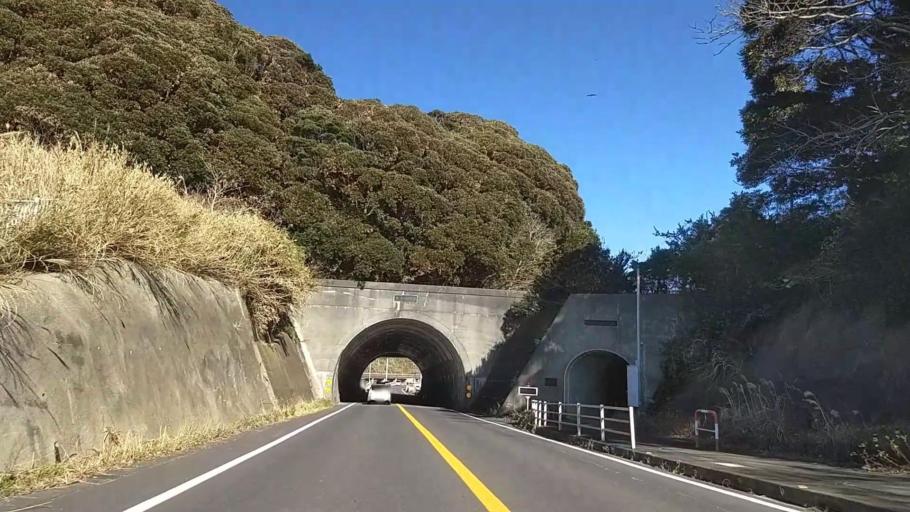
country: JP
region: Chiba
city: Kawaguchi
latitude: 35.0658
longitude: 140.0776
